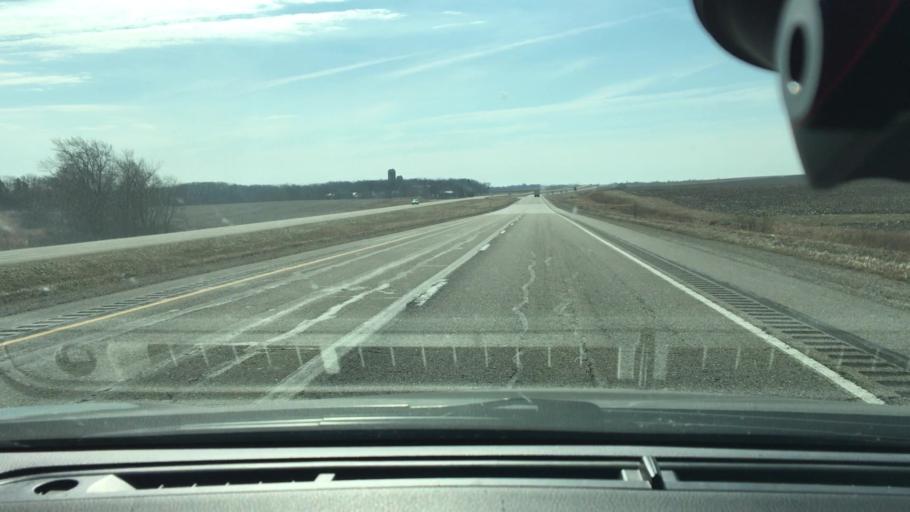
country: US
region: Iowa
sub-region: Chickasaw County
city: Nashua
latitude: 42.9982
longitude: -92.6057
